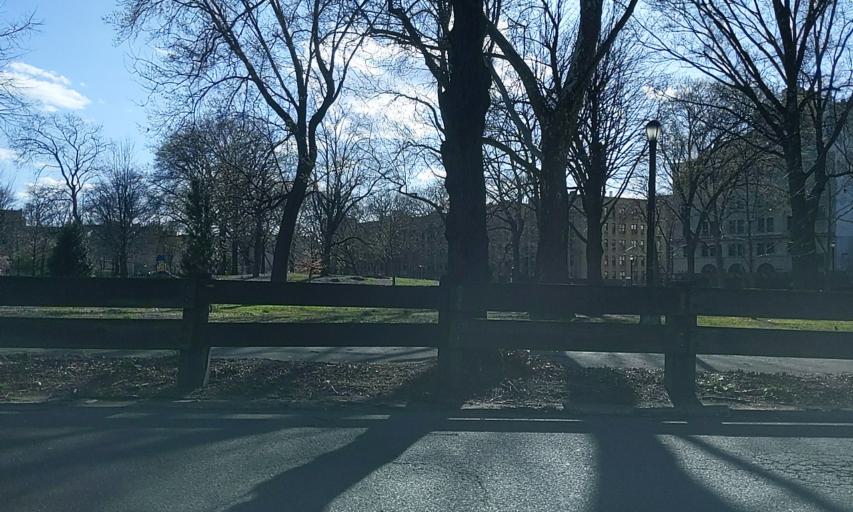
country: US
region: New York
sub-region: Bronx
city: The Bronx
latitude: 40.8368
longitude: -73.8992
